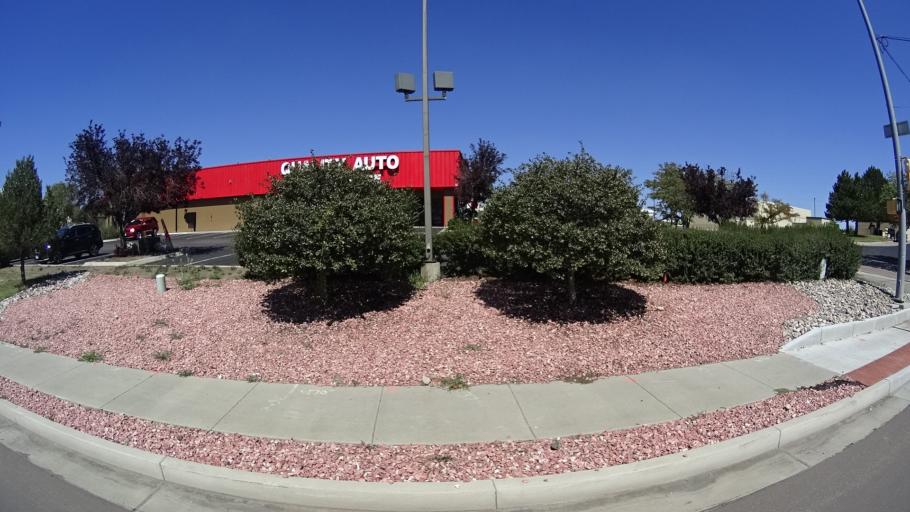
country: US
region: Colorado
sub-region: El Paso County
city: Stratmoor
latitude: 38.8051
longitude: -104.7593
